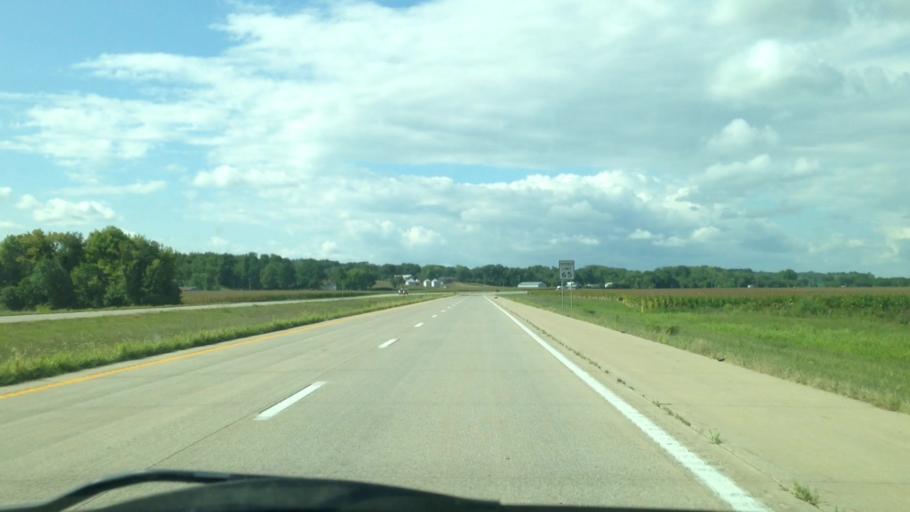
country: US
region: Illinois
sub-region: Hancock County
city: Warsaw
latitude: 40.3282
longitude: -91.5842
